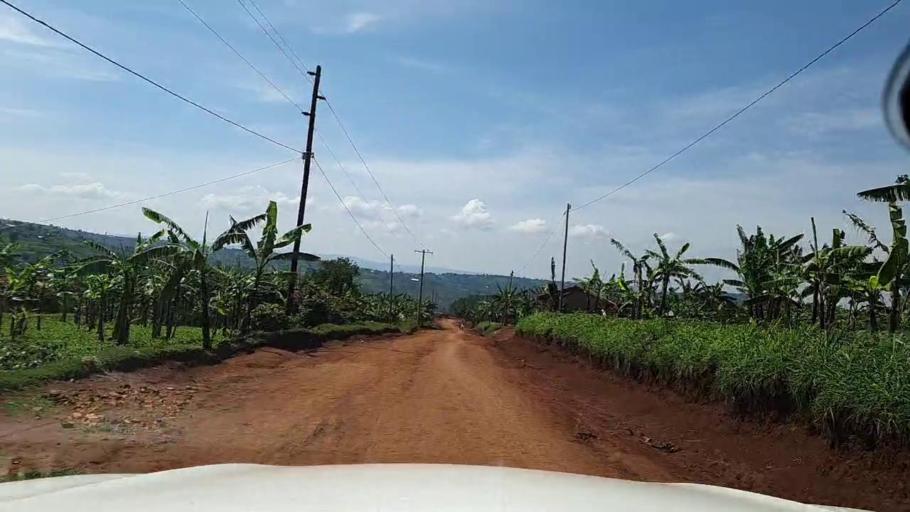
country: RW
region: Southern Province
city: Butare
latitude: -2.7111
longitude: 29.8395
